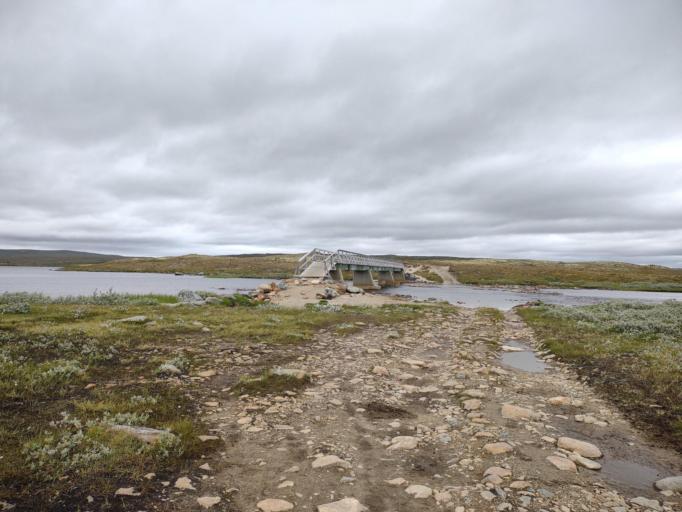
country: NO
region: Hordaland
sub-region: Eidfjord
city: Eidfjord
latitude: 60.2465
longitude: 7.5462
